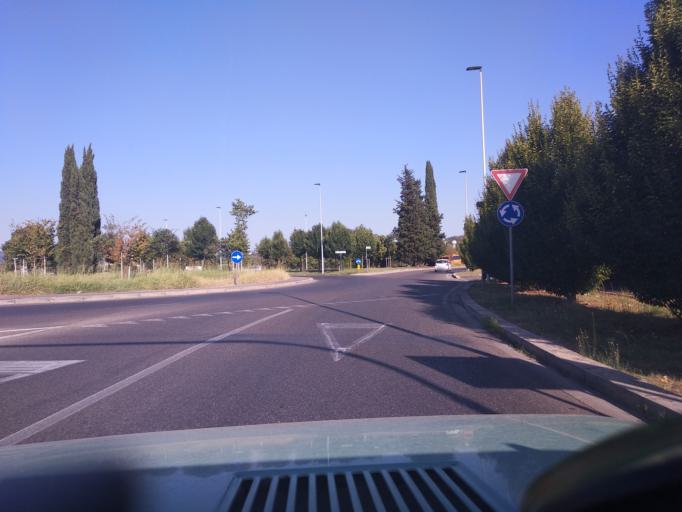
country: IT
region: Tuscany
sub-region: Province of Florence
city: Scandicci
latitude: 43.7635
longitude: 11.1959
